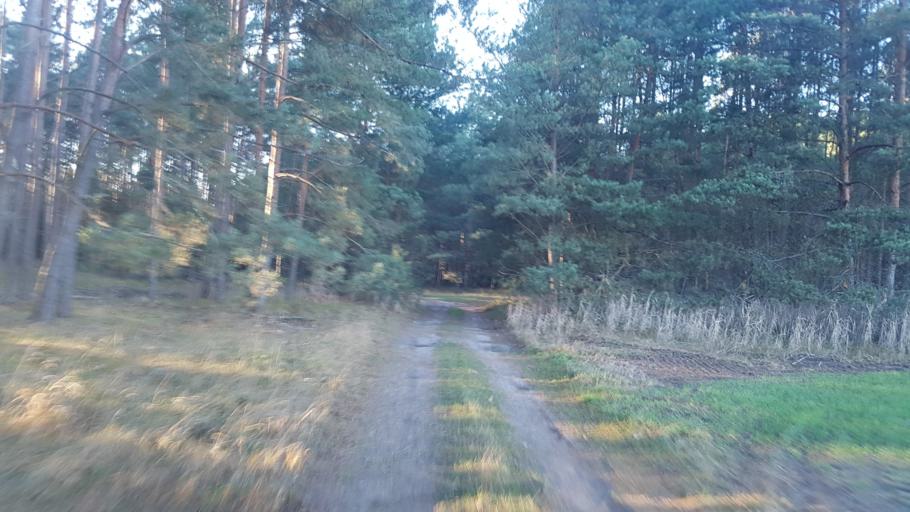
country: DE
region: Brandenburg
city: Drehnow
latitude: 51.8888
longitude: 14.3906
